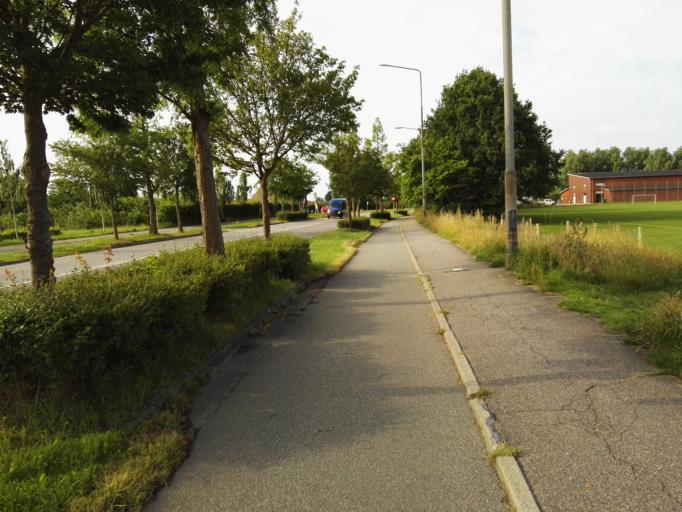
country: DK
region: Capital Region
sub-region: Ballerup Kommune
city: Ballerup
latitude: 55.7441
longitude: 12.3674
